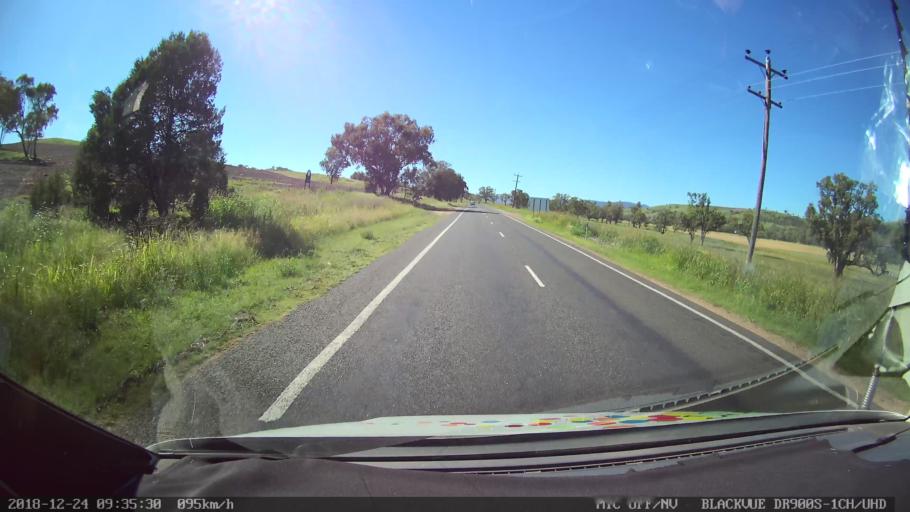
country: AU
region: New South Wales
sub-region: Liverpool Plains
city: Quirindi
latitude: -31.6301
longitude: 150.7177
